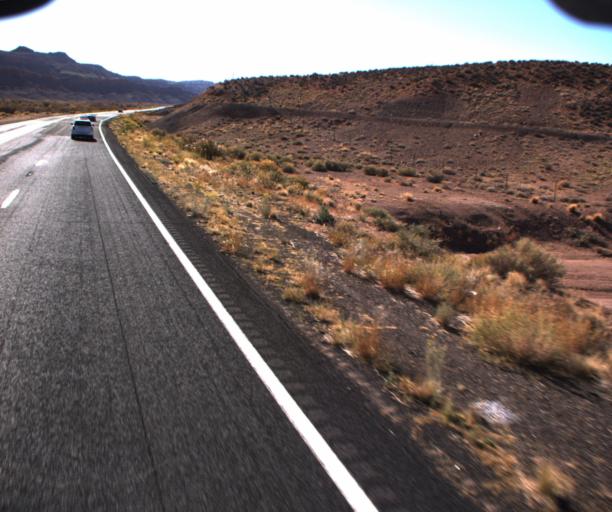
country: US
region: Arizona
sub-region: Coconino County
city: Tuba City
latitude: 36.2276
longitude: -111.4020
